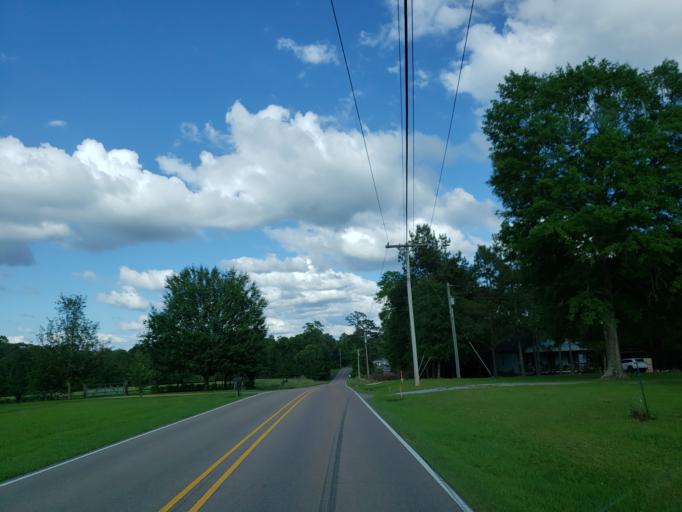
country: US
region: Mississippi
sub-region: Lamar County
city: West Hattiesburg
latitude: 31.2736
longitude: -89.3868
